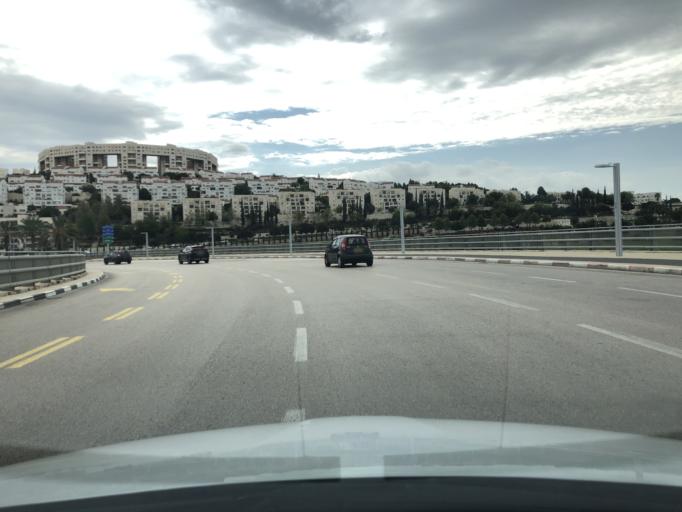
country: IL
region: Central District
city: Modiin
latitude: 31.8996
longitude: 35.0048
